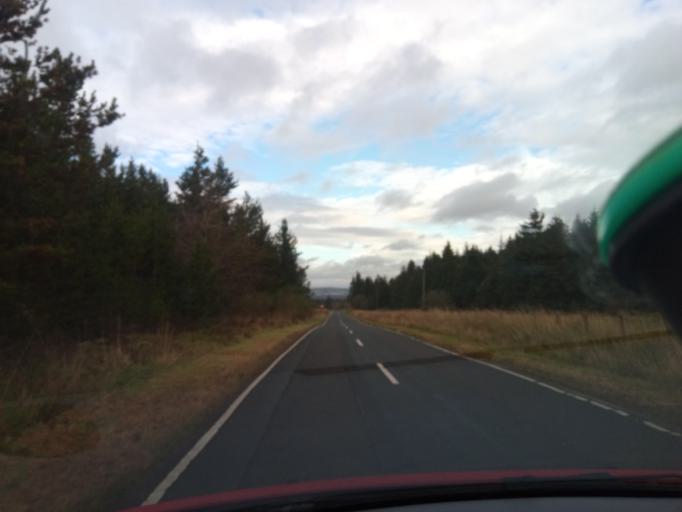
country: GB
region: Scotland
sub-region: West Lothian
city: West Calder
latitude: 55.8141
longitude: -3.5919
